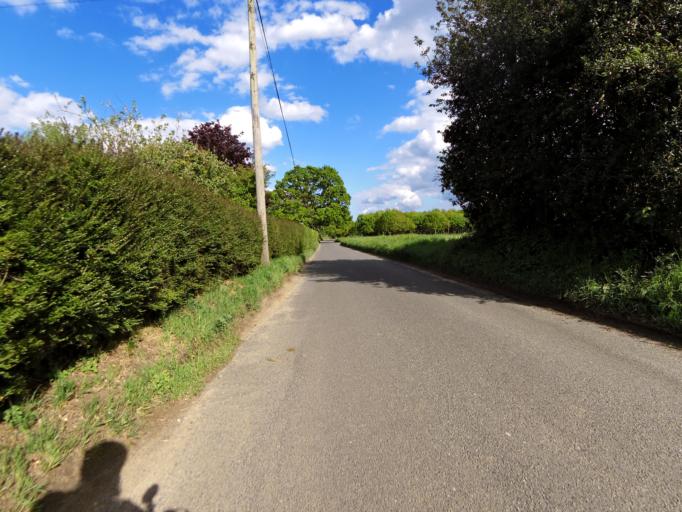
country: GB
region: England
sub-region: Suffolk
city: Woolpit
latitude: 52.2224
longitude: 0.8586
